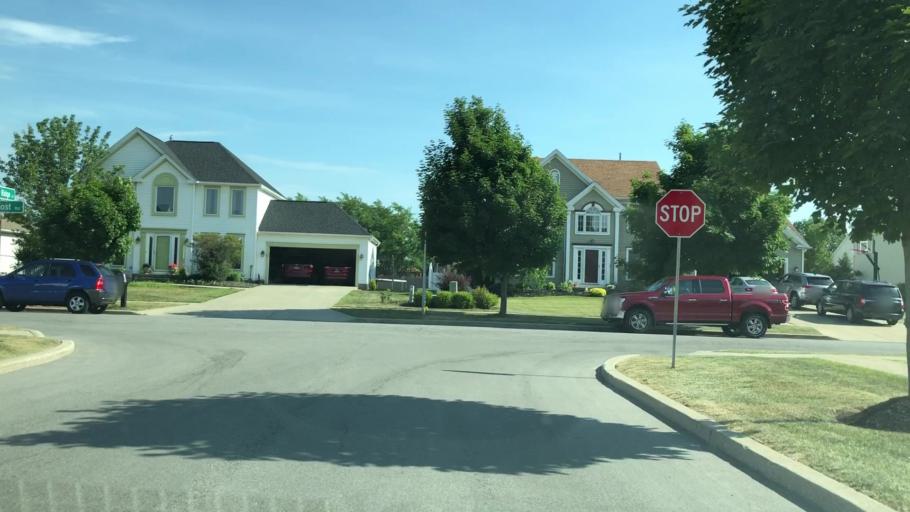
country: US
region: New York
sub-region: Erie County
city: Lancaster
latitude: 42.8779
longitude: -78.6817
